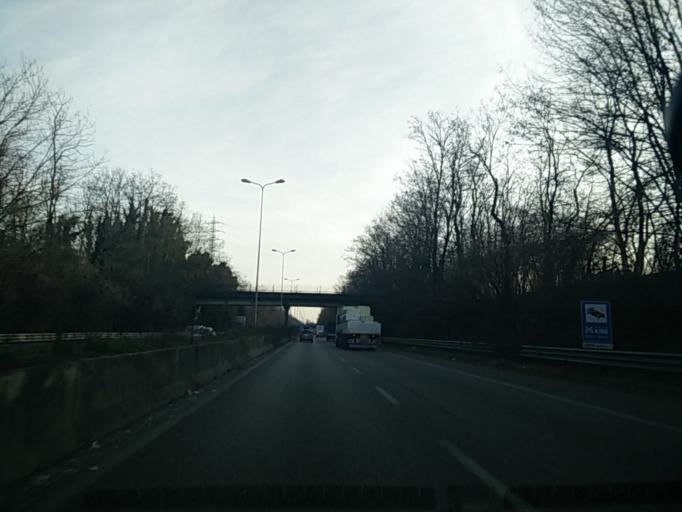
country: IT
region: Lombardy
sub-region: Provincia di Monza e Brianza
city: Varedo
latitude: 45.6069
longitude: 9.1666
